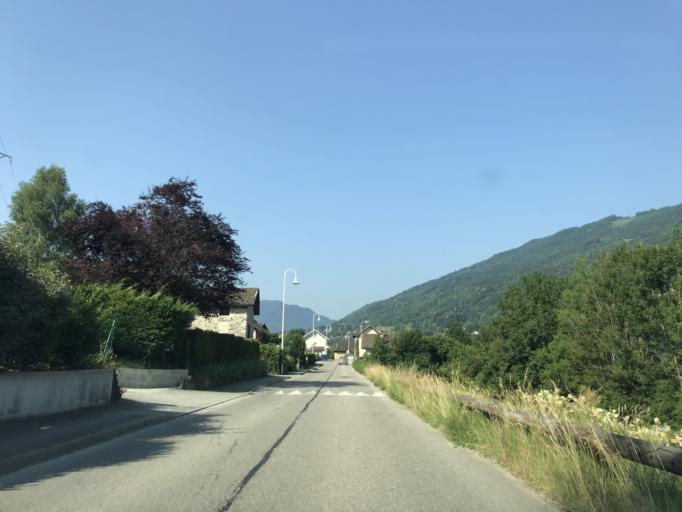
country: FR
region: Rhone-Alpes
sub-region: Departement de l'Isere
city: Allevard
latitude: 45.4058
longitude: 6.0861
